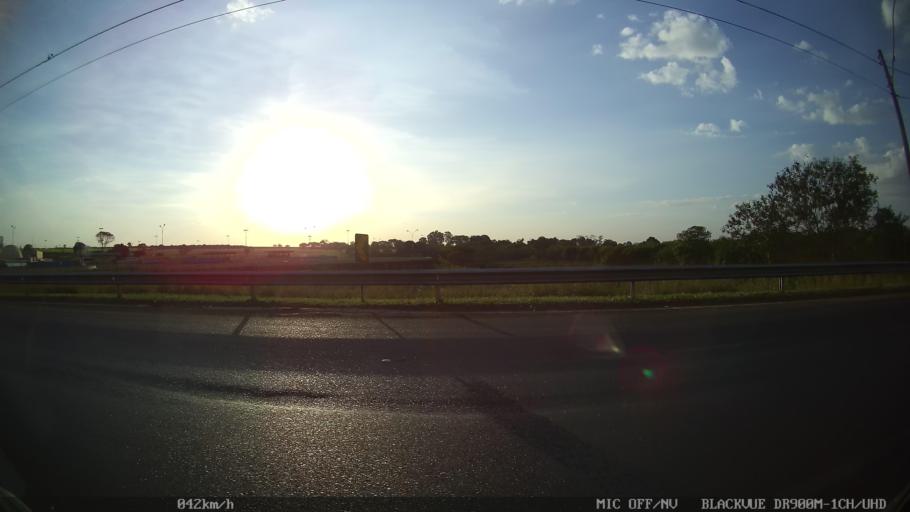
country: BR
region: Sao Paulo
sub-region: Ribeirao Preto
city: Ribeirao Preto
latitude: -21.1045
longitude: -47.8103
